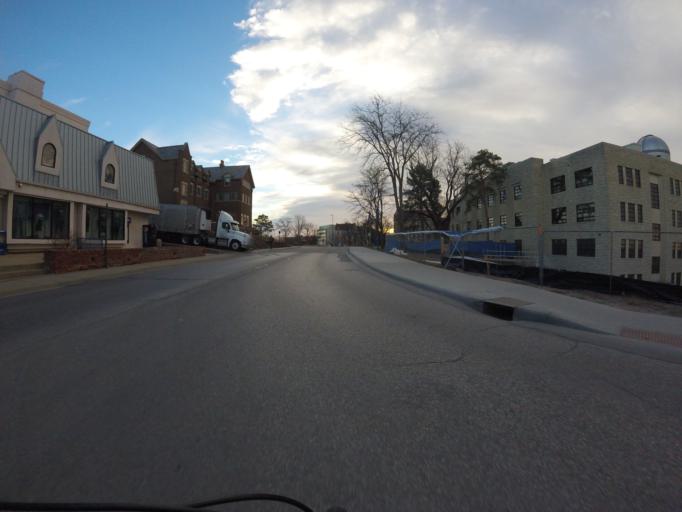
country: US
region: Kansas
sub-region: Douglas County
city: Lawrence
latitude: 38.9508
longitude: -95.2608
